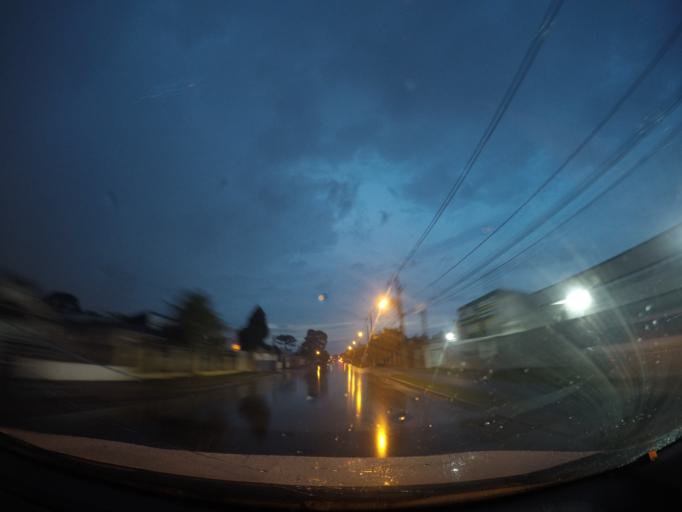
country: BR
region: Parana
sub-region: Sao Jose Dos Pinhais
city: Sao Jose dos Pinhais
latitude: -25.4978
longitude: -49.2353
